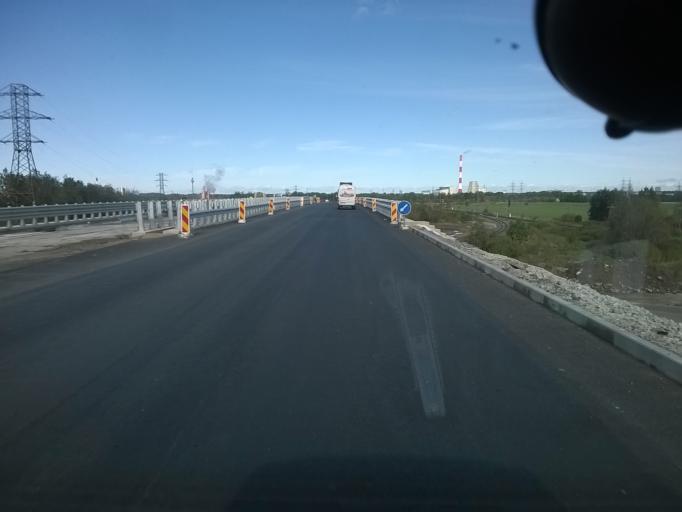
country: EE
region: Harju
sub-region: Joelaehtme vald
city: Loo
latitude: 59.4248
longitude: 24.9209
